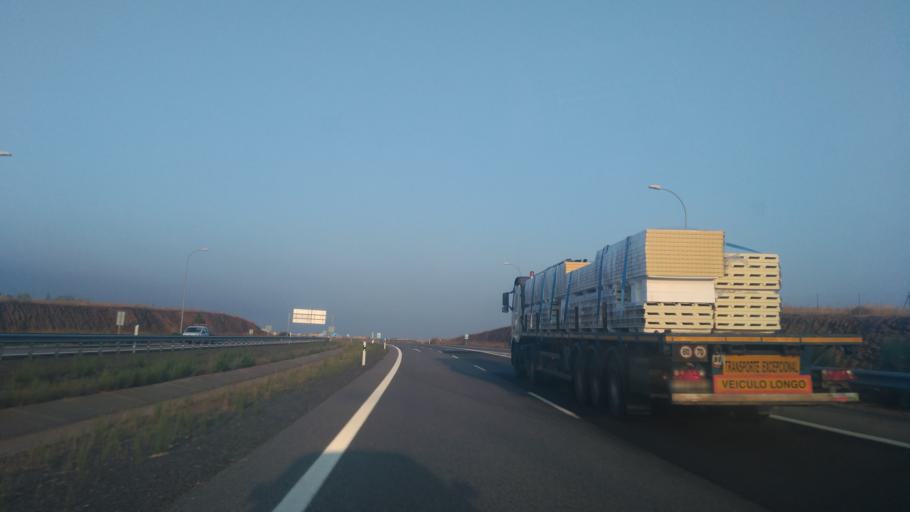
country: ES
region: Castille and Leon
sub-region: Provincia de Salamanca
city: Doninos de Salamanca
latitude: 40.9571
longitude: -5.7198
